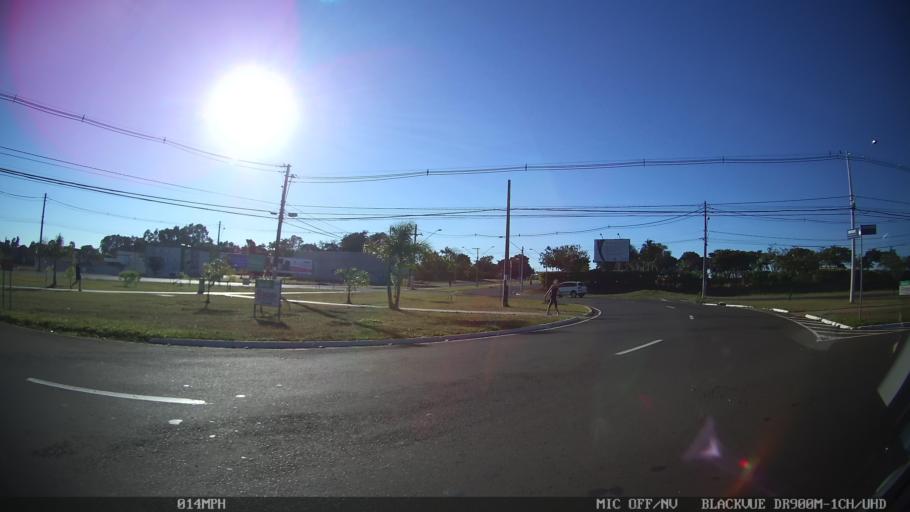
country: BR
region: Sao Paulo
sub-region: Franca
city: Franca
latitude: -20.5642
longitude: -47.3645
